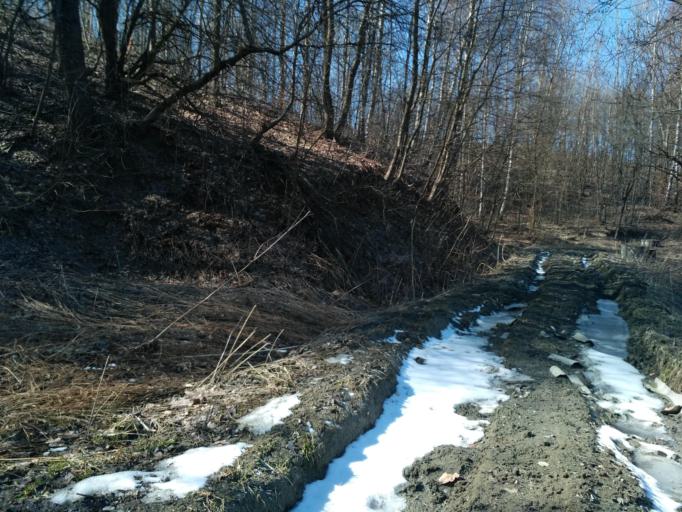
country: PL
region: Subcarpathian Voivodeship
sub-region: Powiat brzozowski
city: Golcowa
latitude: 49.7602
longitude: 22.0315
